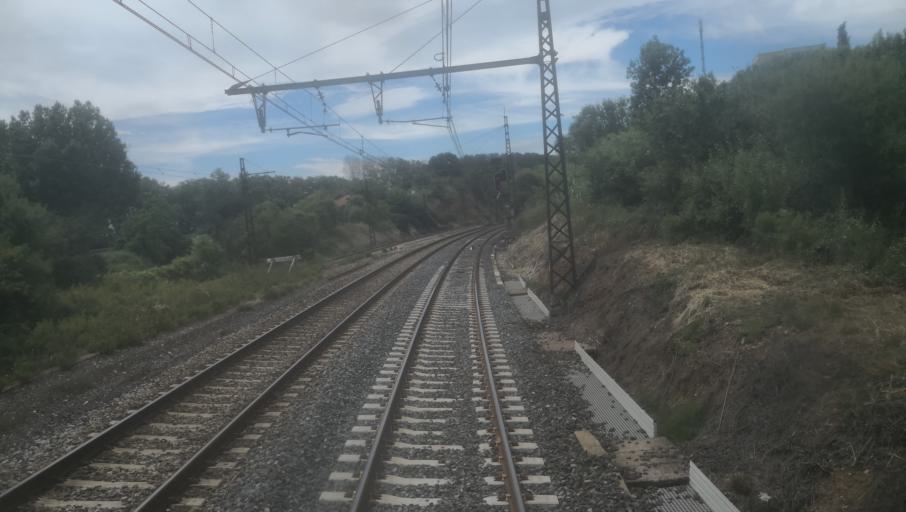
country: FR
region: Languedoc-Roussillon
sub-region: Departement de l'Herault
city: Villeneuve-les-Beziers
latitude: 43.3241
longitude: 3.2504
